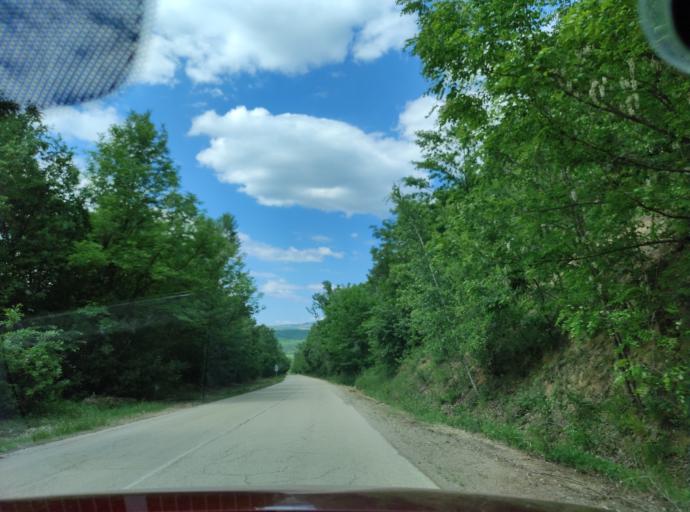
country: BG
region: Montana
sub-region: Obshtina Montana
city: Montana
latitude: 43.3873
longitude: 23.0769
